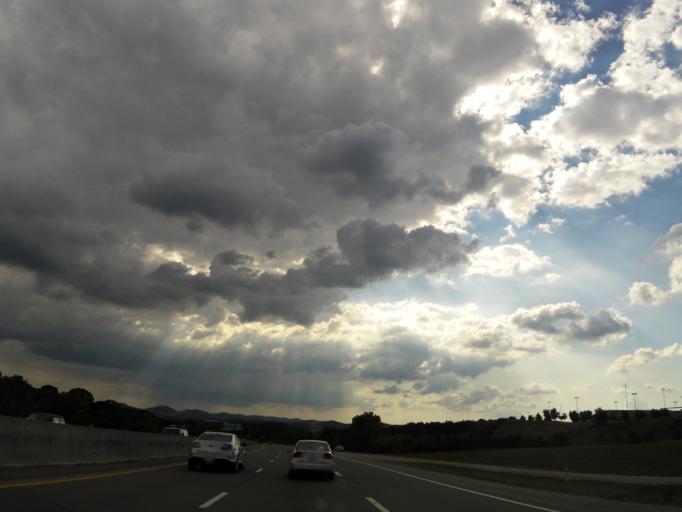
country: US
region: Tennessee
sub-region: Davidson County
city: Nashville
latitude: 36.2417
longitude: -86.7593
